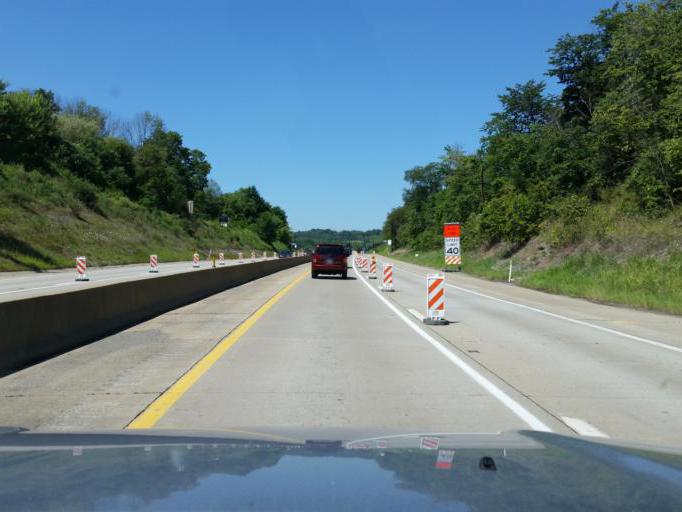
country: US
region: Pennsylvania
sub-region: Westmoreland County
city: Latrobe
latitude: 40.3959
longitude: -79.4355
